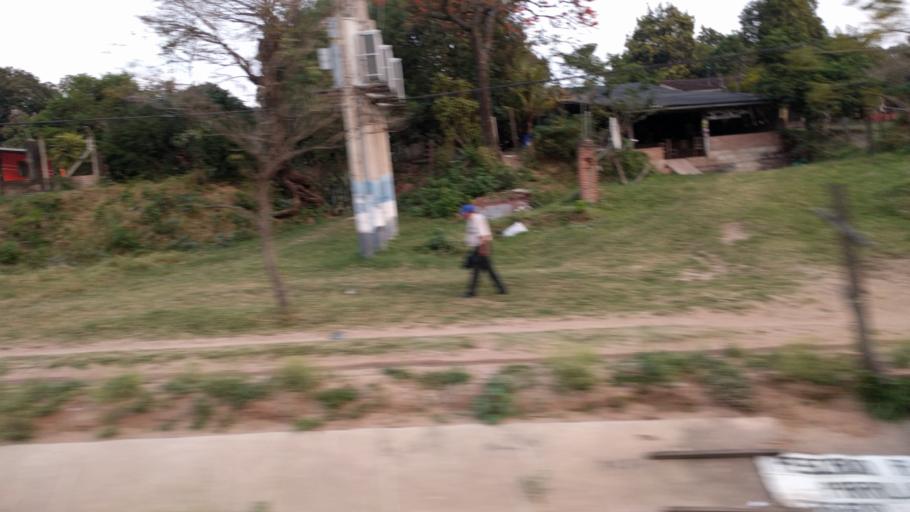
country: BO
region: Santa Cruz
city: Santa Rita
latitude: -17.8940
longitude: -63.3343
